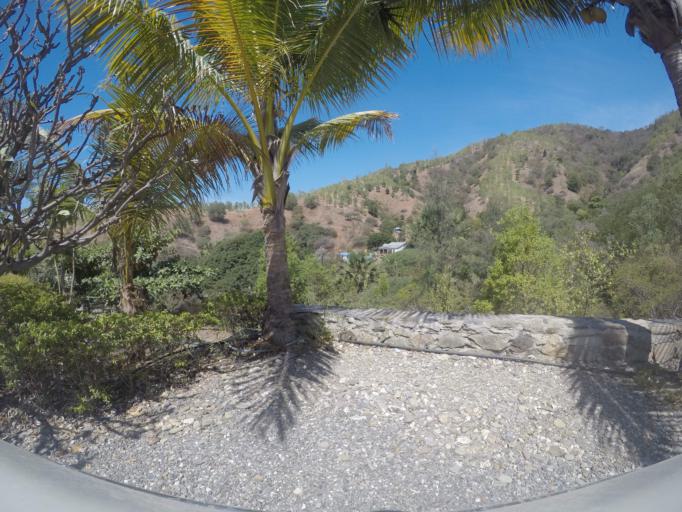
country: TL
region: Dili
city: Dili
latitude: -8.5760
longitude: 125.4743
